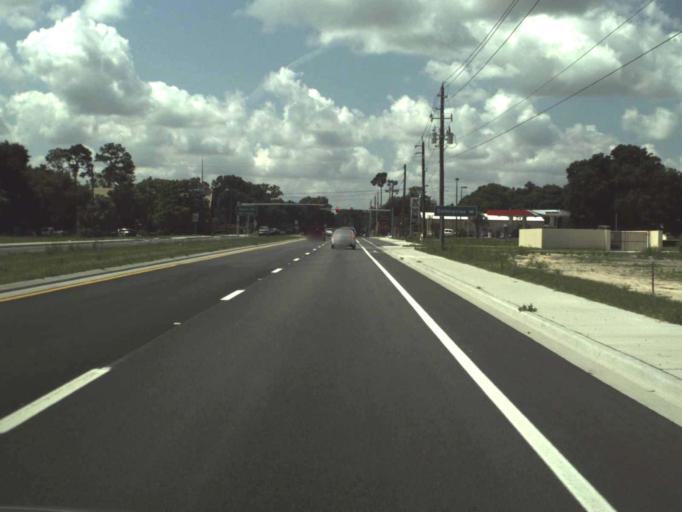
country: US
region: Florida
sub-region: Seminole County
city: Midway
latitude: 28.8523
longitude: -81.1622
